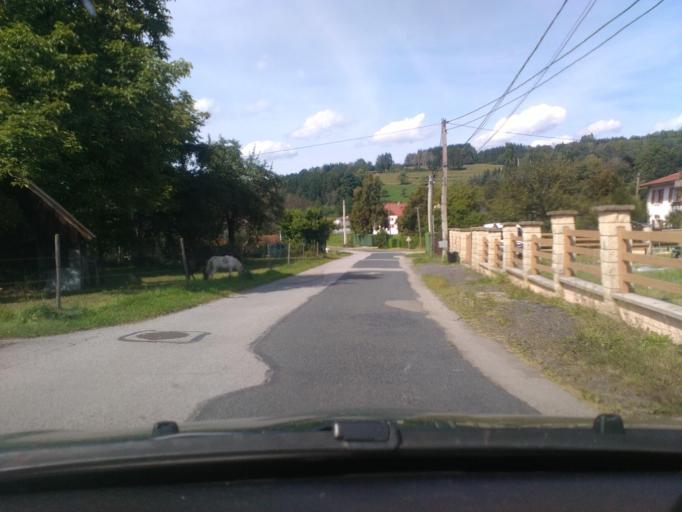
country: FR
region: Lorraine
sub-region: Departement des Vosges
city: Fraize
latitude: 48.2153
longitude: 7.0107
